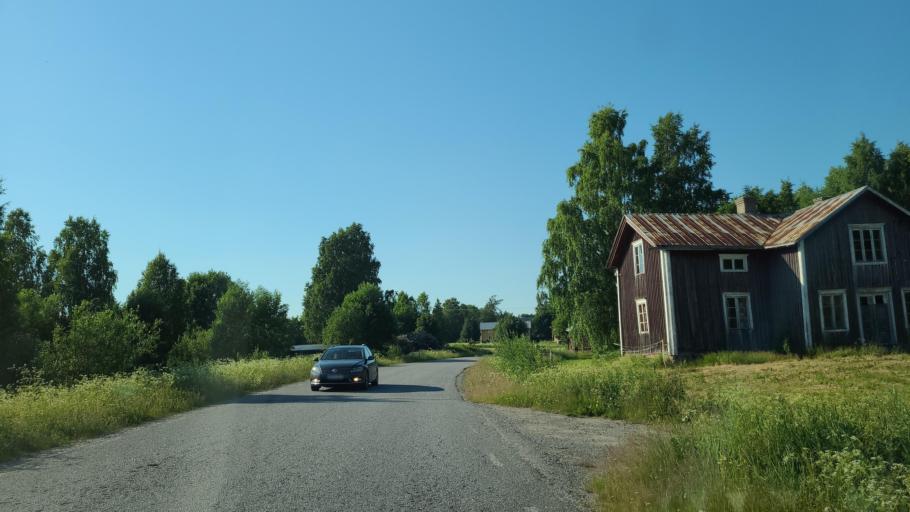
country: SE
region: Vaesterbotten
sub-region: Robertsfors Kommun
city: Robertsfors
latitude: 64.3027
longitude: 20.7792
